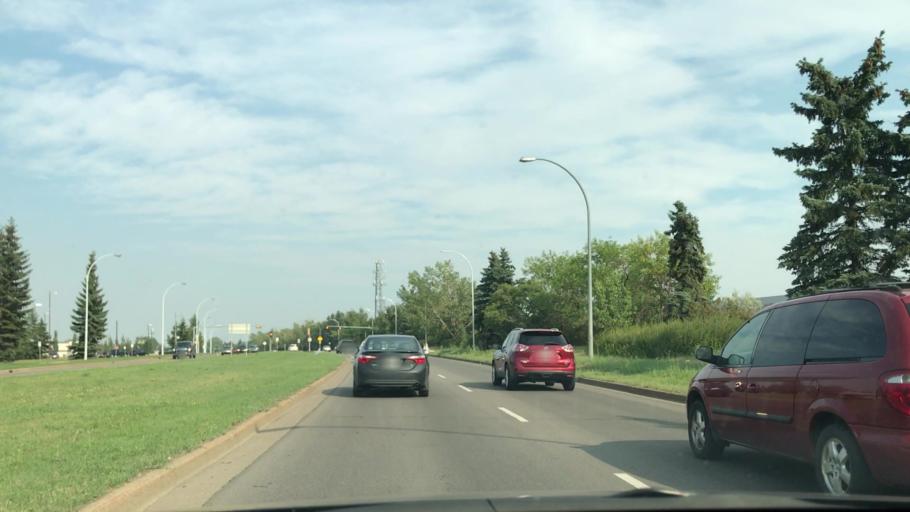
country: CA
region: Alberta
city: Edmonton
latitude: 53.4522
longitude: -113.4765
